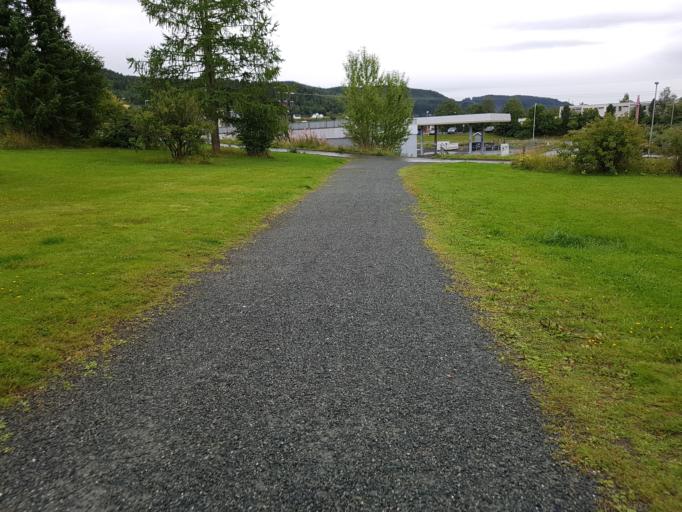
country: NO
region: Sor-Trondelag
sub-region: Trondheim
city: Trondheim
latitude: 63.3921
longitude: 10.4316
